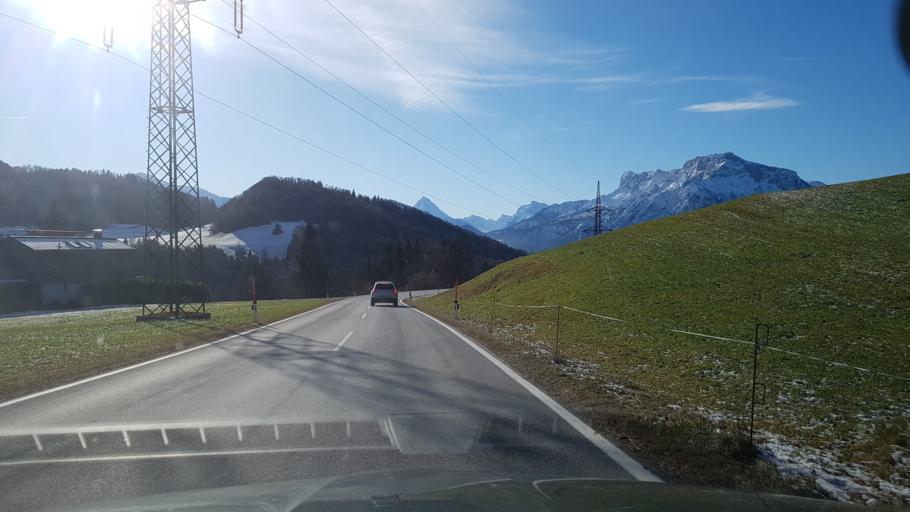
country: AT
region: Salzburg
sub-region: Politischer Bezirk Salzburg-Umgebung
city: Elsbethen
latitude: 47.7721
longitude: 13.1073
